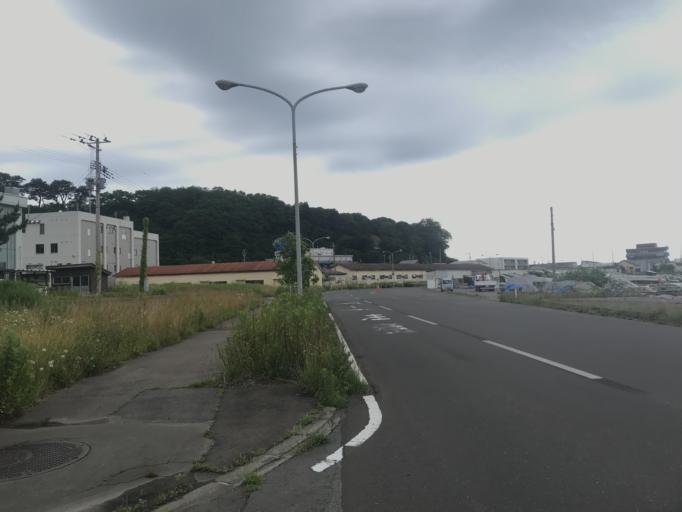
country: JP
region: Aomori
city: Shimokizukuri
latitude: 40.7804
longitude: 140.2085
